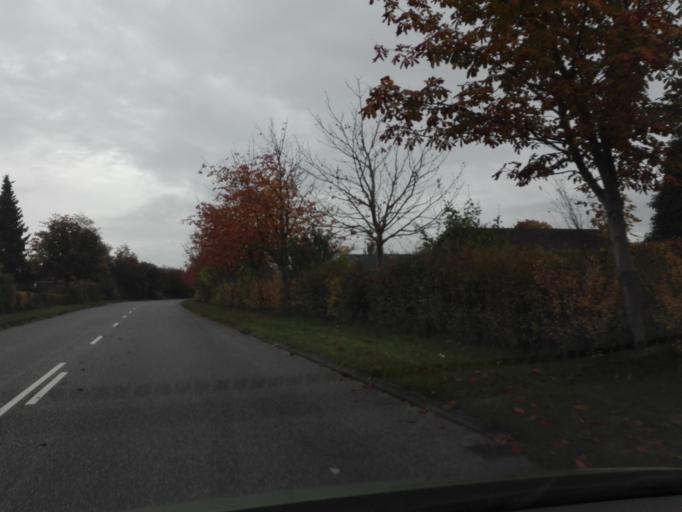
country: DK
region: Central Jutland
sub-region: Arhus Kommune
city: Kolt
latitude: 56.1054
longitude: 10.0688
